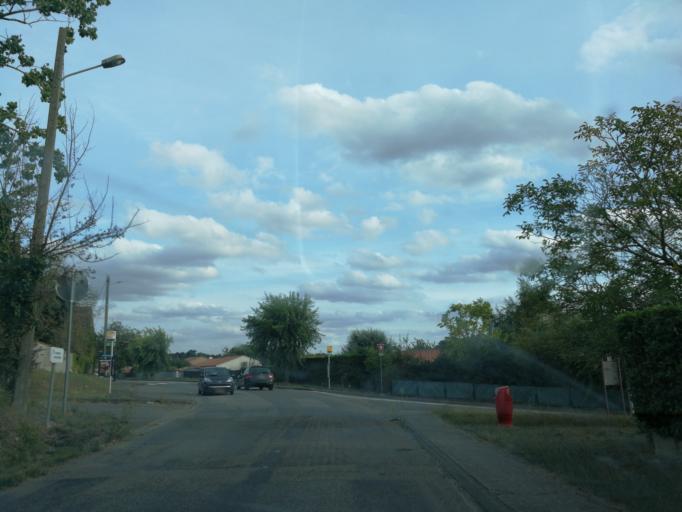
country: FR
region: Midi-Pyrenees
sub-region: Departement de la Haute-Garonne
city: Flourens
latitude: 43.5932
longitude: 1.5731
